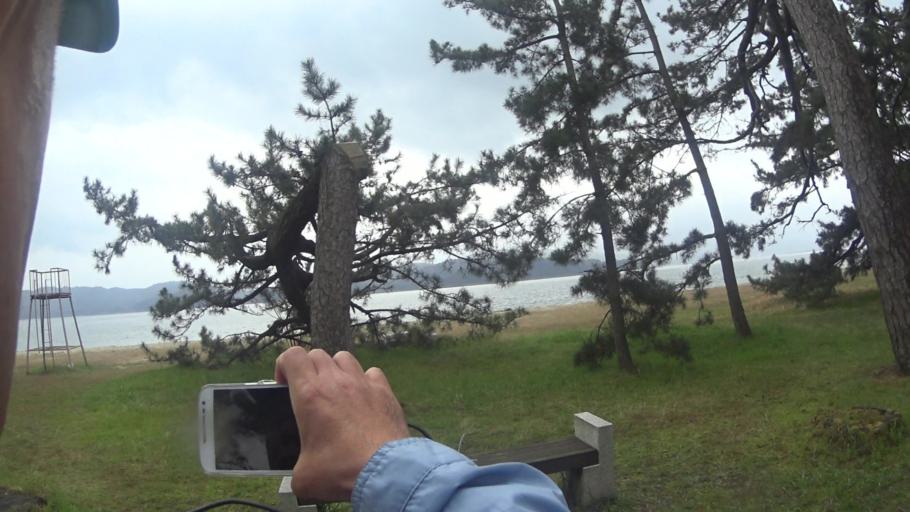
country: JP
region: Kyoto
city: Miyazu
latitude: 35.5755
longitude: 135.1983
